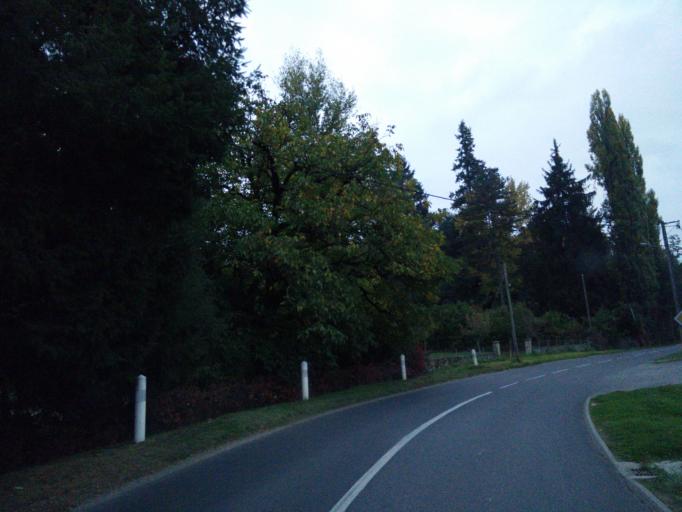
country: FR
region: Aquitaine
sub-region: Departement de la Dordogne
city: Carsac-Aillac
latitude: 44.8390
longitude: 1.2765
